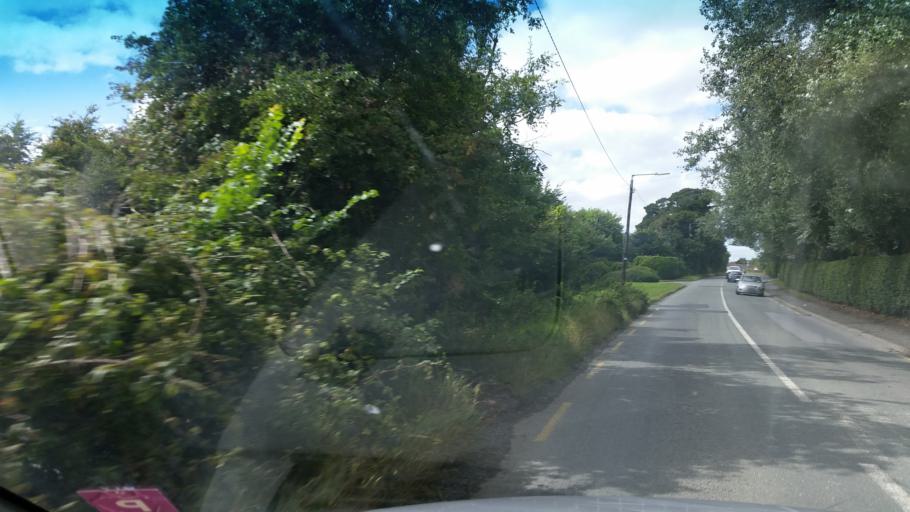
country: IE
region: Leinster
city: Kinsealy-Drinan
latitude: 53.4340
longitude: -6.1816
